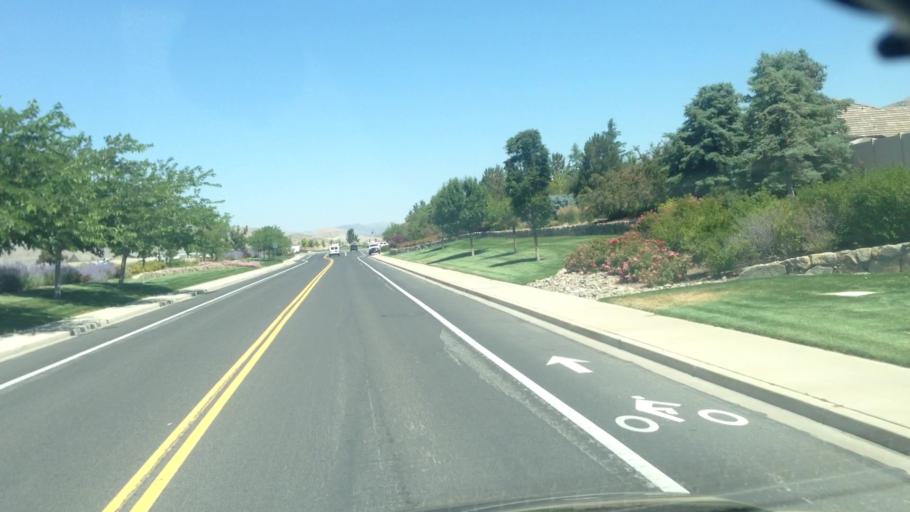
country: US
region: Nevada
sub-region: Washoe County
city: Sparks
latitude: 39.4295
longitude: -119.7163
